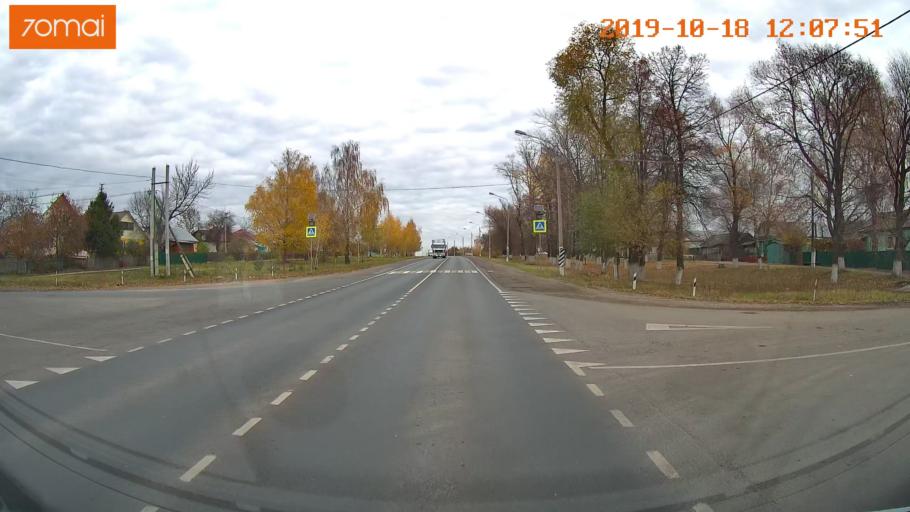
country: RU
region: Rjazan
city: Zakharovo
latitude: 54.3716
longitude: 39.2857
